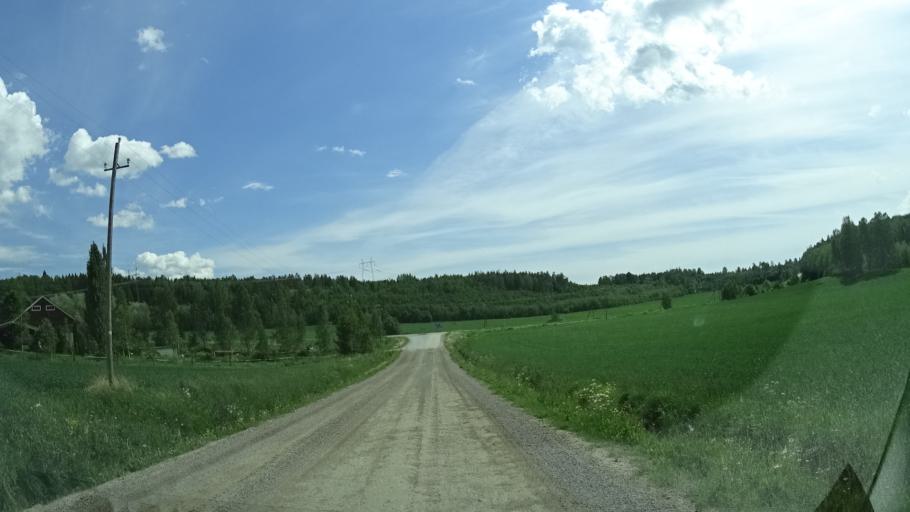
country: FI
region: Uusimaa
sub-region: Helsinki
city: Siuntio
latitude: 60.1963
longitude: 24.2518
